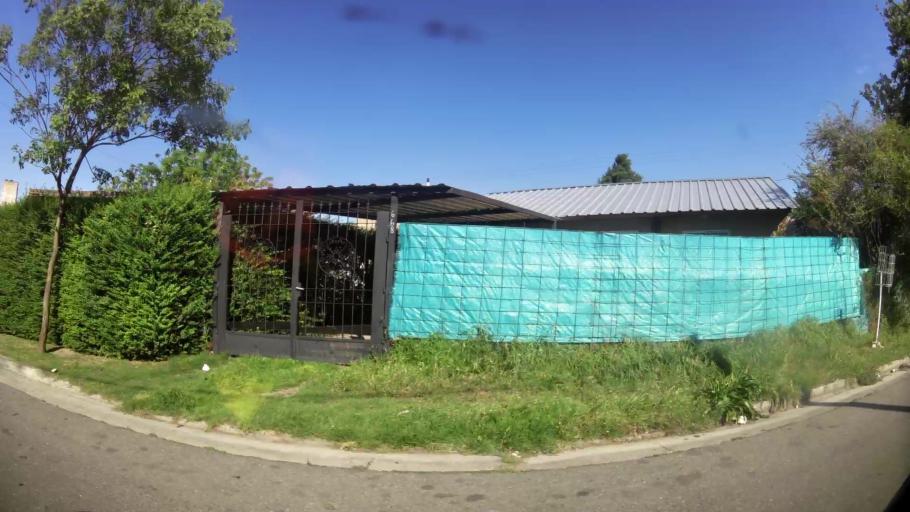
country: AR
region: Cordoba
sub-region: Departamento de Capital
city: Cordoba
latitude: -31.3648
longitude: -64.1914
